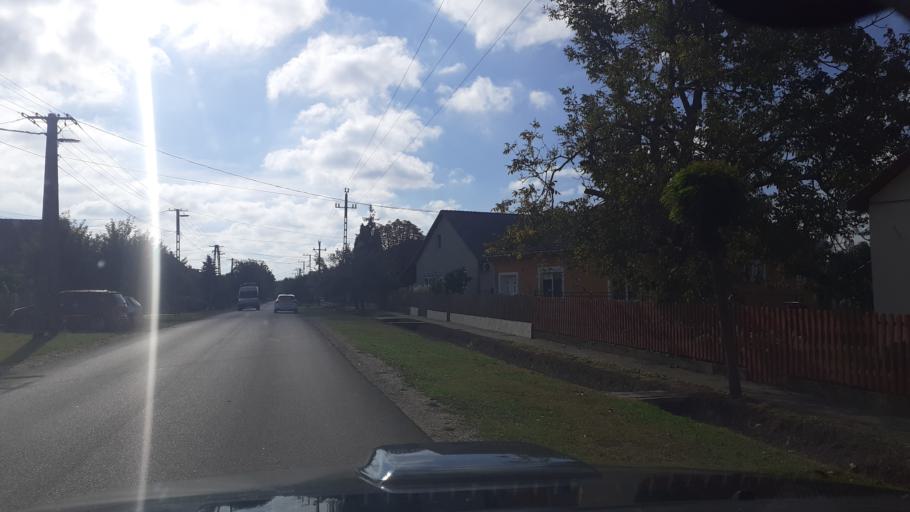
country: HU
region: Fejer
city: dunaujvaros
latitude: 46.9533
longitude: 18.8547
